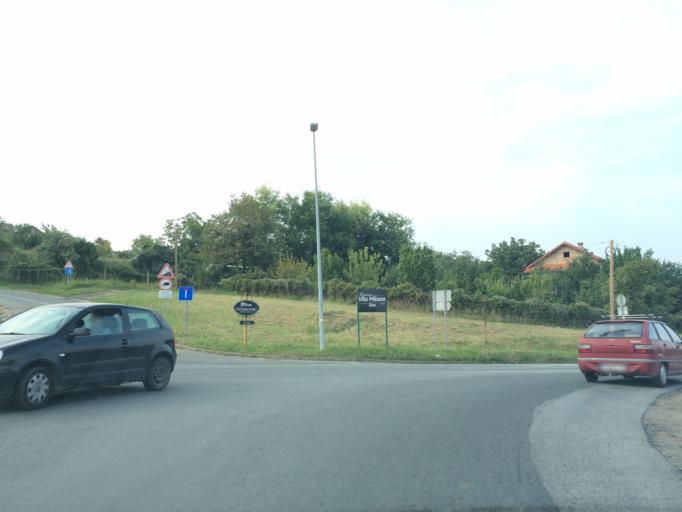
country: RS
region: Autonomna Pokrajina Vojvodina
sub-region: Juznobacki Okrug
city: Novi Sad
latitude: 45.2214
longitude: 19.8340
